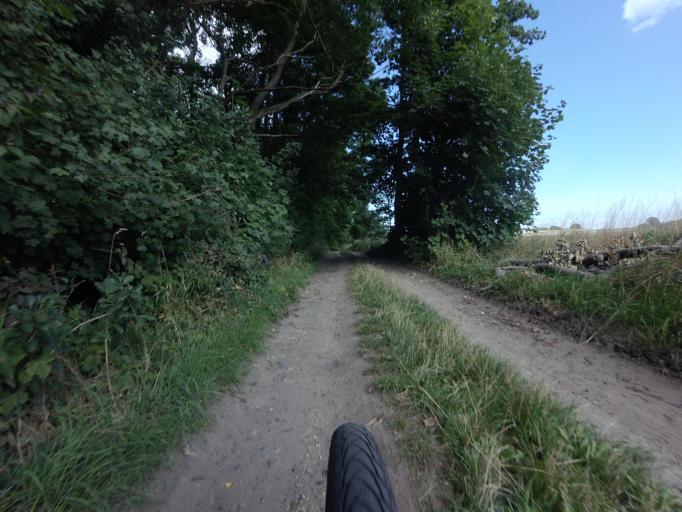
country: DK
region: Zealand
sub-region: Vordingborg Kommune
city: Stege
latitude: 54.9681
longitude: 12.4150
